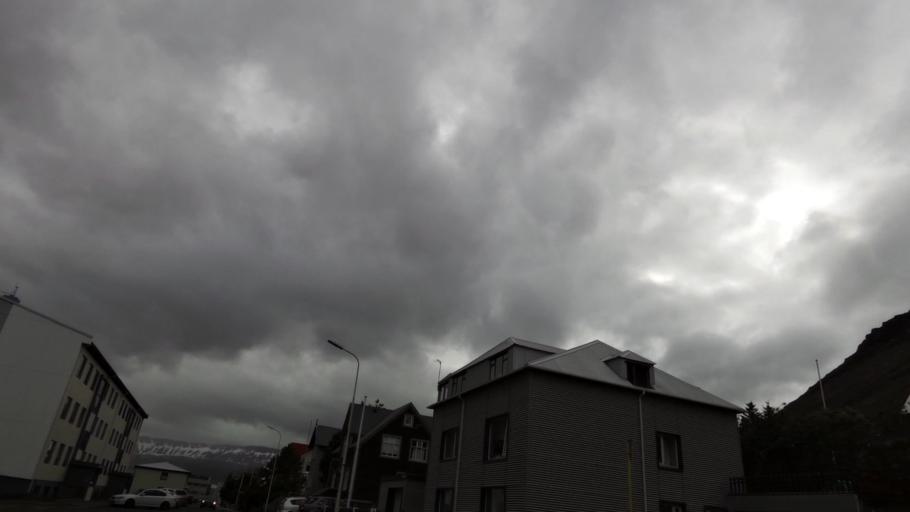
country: IS
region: Westfjords
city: Isafjoerdur
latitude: 66.0780
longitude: -23.1263
